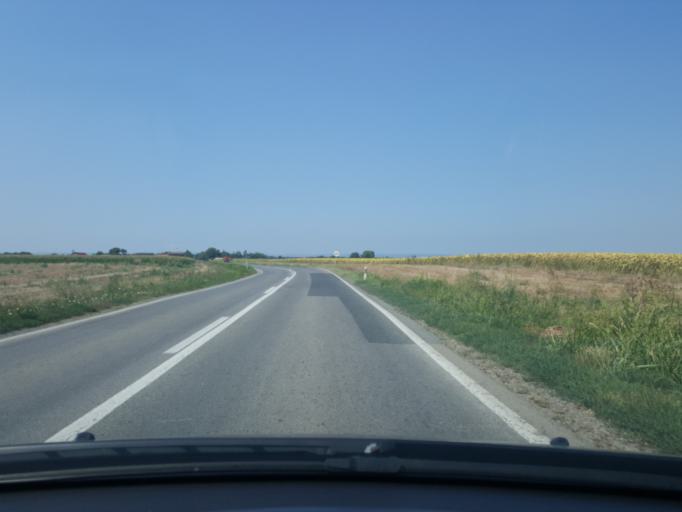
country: RS
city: Hrtkovci
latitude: 44.8614
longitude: 19.7718
